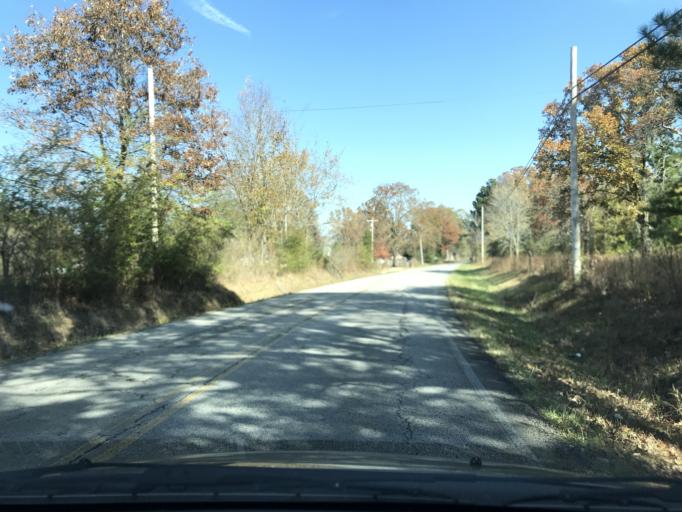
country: US
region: Tennessee
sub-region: Coffee County
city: Tullahoma
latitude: 35.3971
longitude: -86.1637
